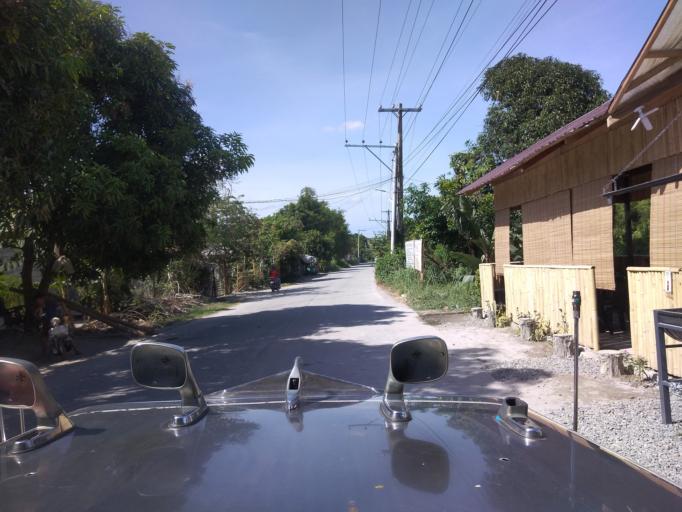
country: PH
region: Central Luzon
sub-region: Province of Pampanga
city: Magliman
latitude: 15.0219
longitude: 120.6546
